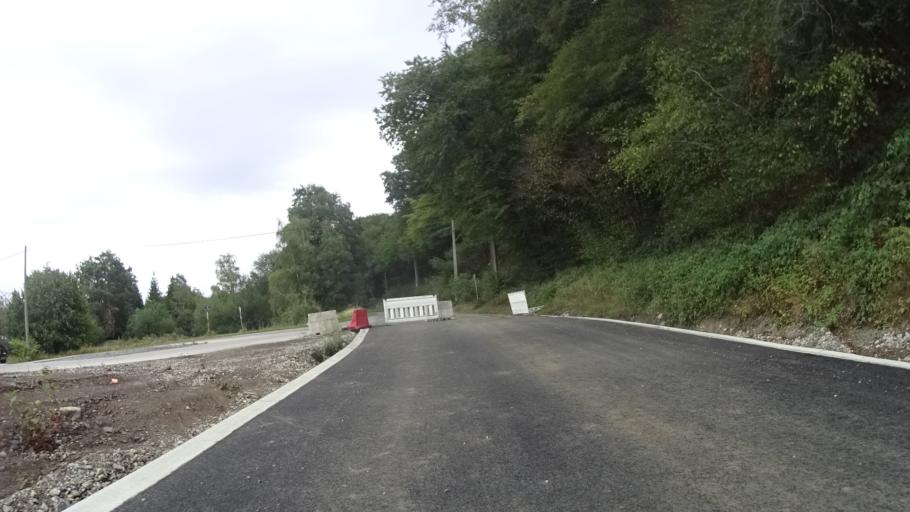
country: BE
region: Wallonia
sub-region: Province de Liege
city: Amay
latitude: 50.5322
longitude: 5.3130
